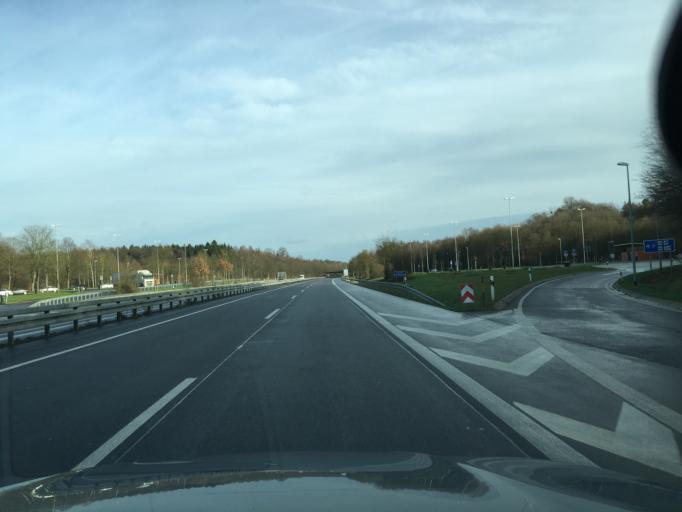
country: DE
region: North Rhine-Westphalia
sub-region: Regierungsbezirk Koln
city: Weilerswist
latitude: 50.7853
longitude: 6.8424
